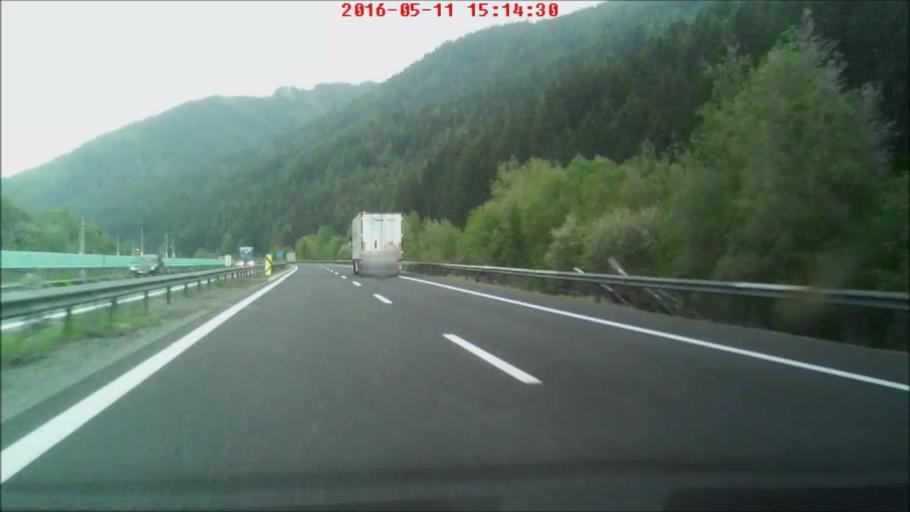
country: AT
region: Styria
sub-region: Politischer Bezirk Leoben
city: Kammern im Liesingtal
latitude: 47.3904
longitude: 14.8795
